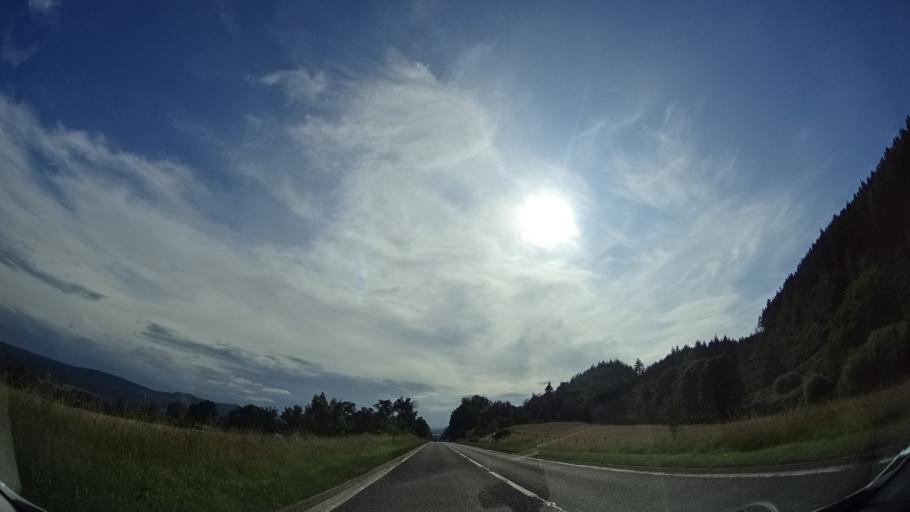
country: GB
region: Scotland
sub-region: Highland
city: Conon Bridge
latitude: 57.5633
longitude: -4.4856
